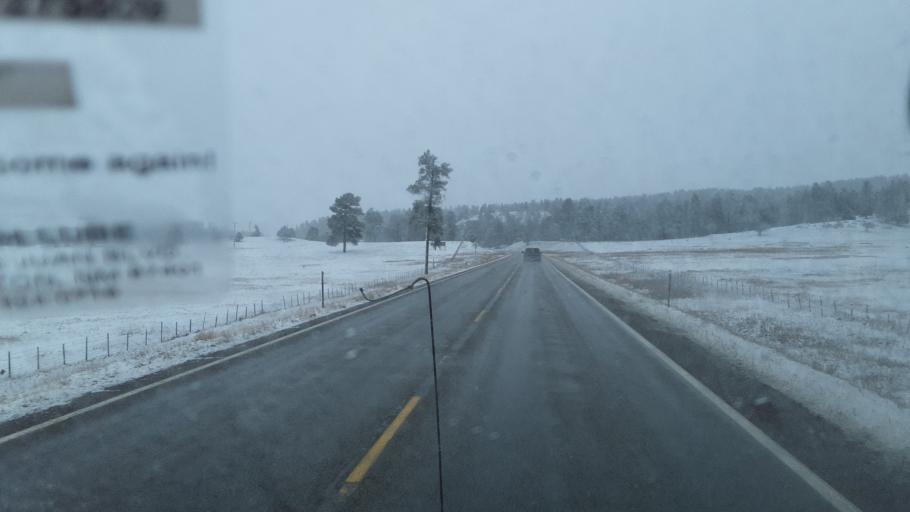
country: US
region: Colorado
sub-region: Archuleta County
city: Pagosa Springs
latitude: 37.1997
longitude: -106.9614
